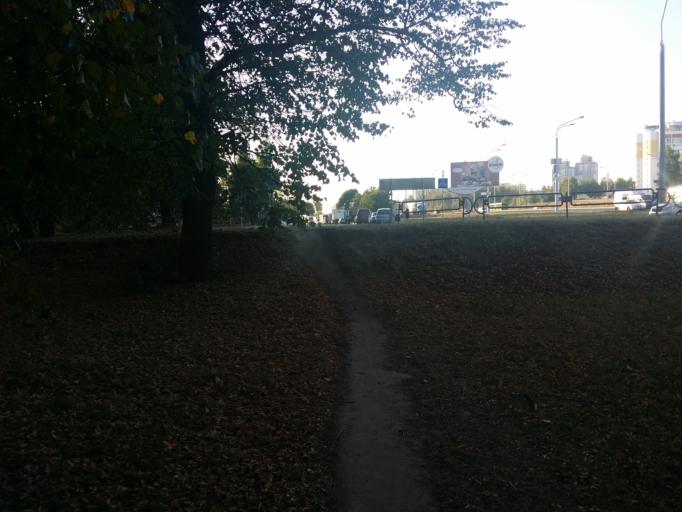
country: BY
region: Minsk
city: Vyaliki Trastsyanets
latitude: 53.8560
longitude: 27.6882
